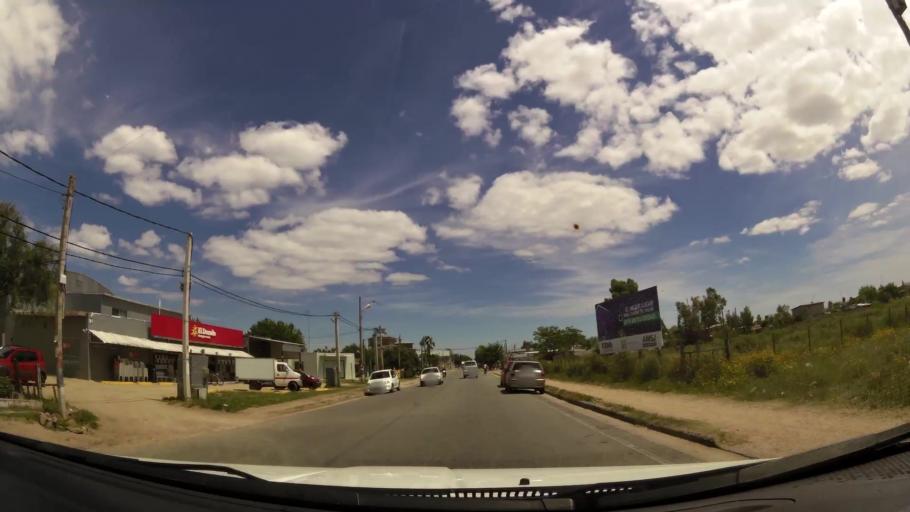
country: UY
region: San Jose
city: Delta del Tigre
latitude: -34.7412
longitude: -56.4502
